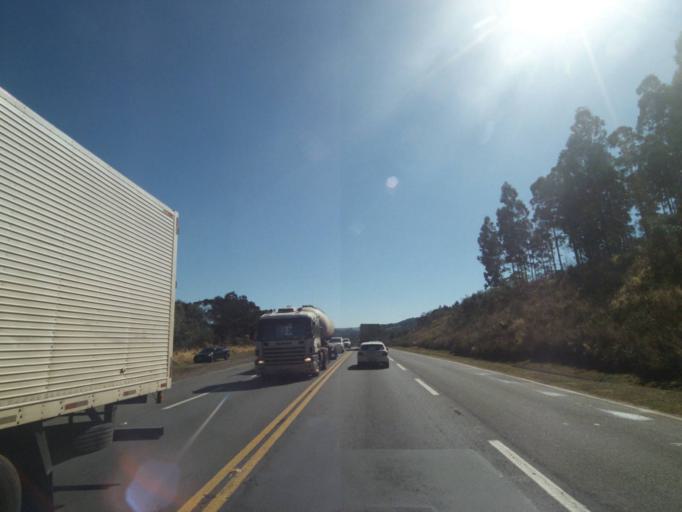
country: BR
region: Parana
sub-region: Tibagi
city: Tibagi
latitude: -24.6853
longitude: -50.5918
